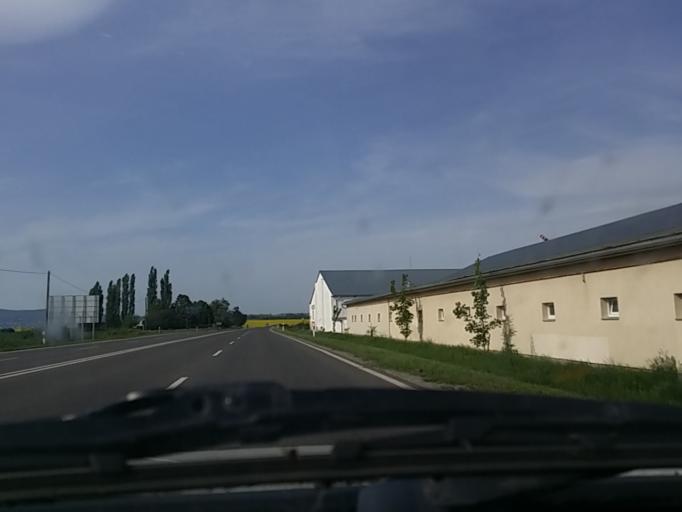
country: HU
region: Baranya
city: Kozarmisleny
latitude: 45.9951
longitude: 18.2329
